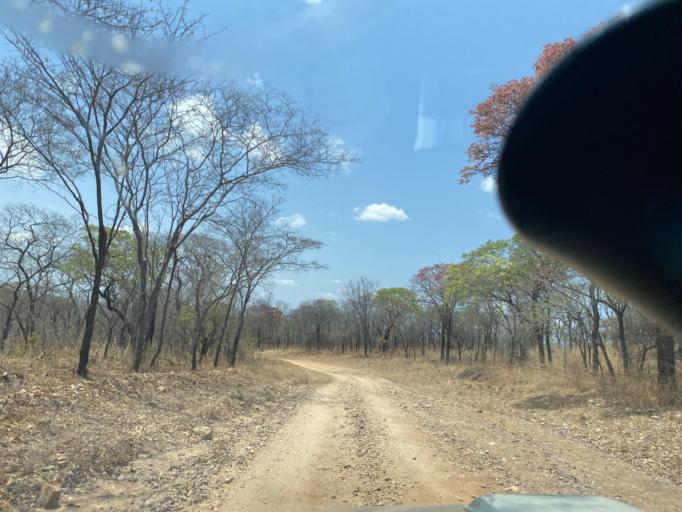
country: ZM
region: Lusaka
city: Luangwa
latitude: -15.0089
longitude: 29.7335
